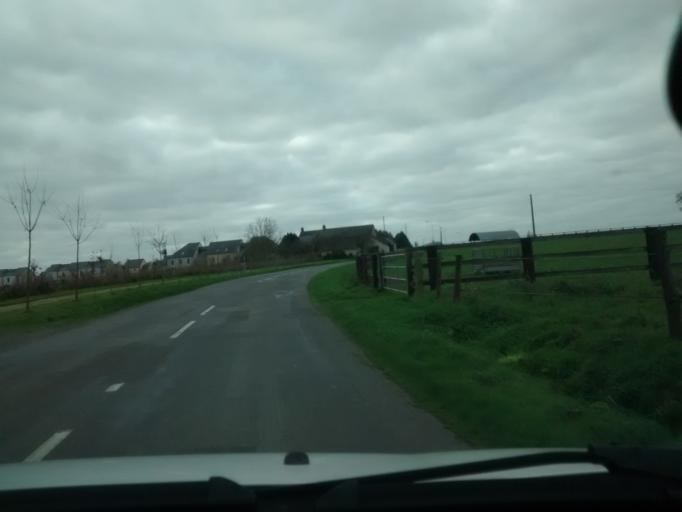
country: FR
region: Brittany
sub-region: Departement d'Ille-et-Vilaine
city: Le Rheu
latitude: 48.0852
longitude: -1.7740
